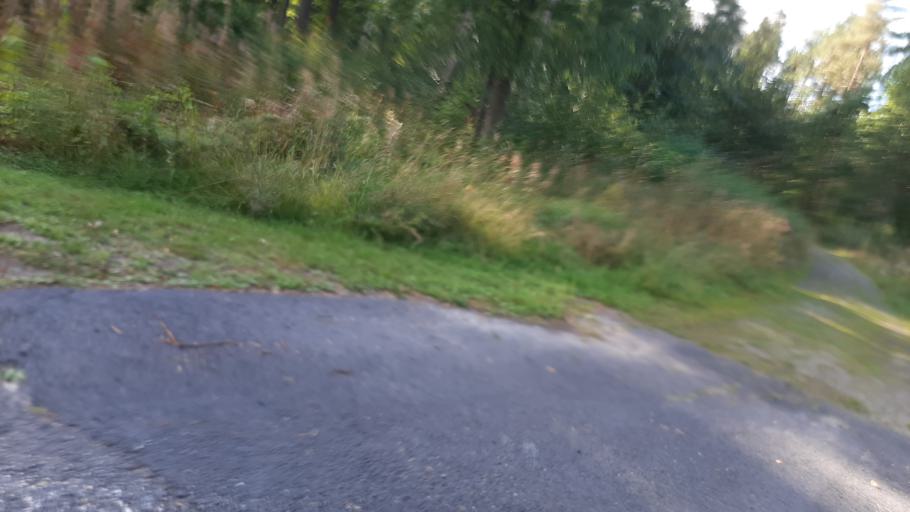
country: FI
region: North Karelia
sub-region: Joensuu
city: Joensuu
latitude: 62.6203
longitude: 29.7834
